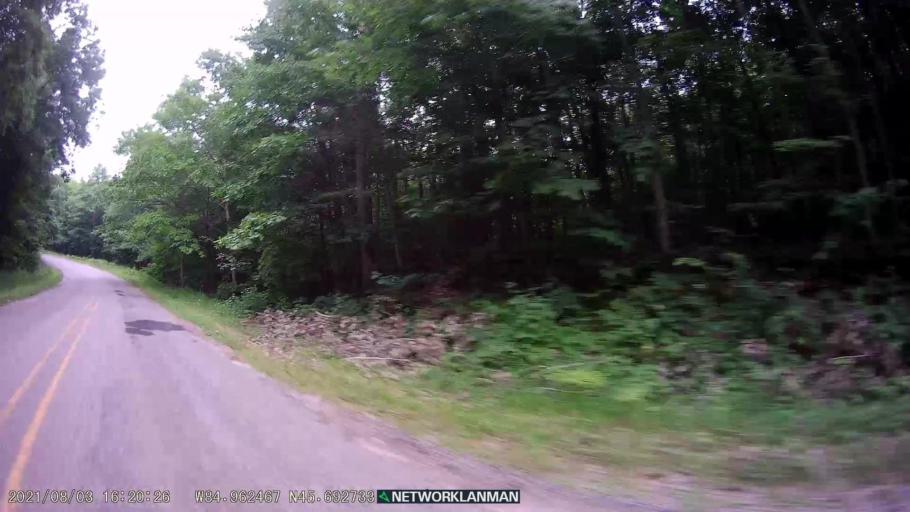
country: US
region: Michigan
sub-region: Emmet County
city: Harbor Springs
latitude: 45.6937
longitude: -84.9629
